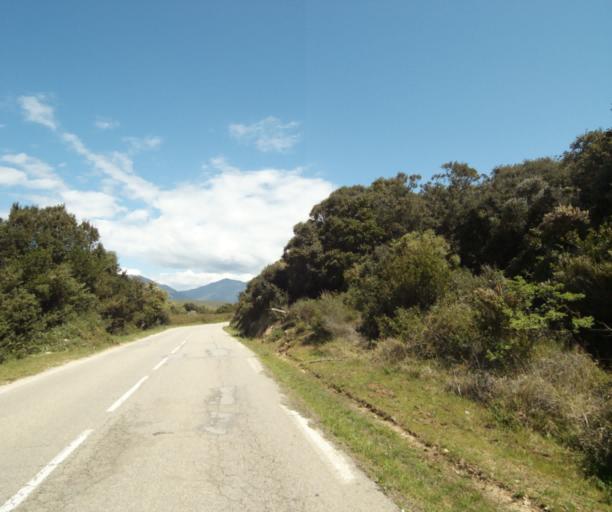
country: FR
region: Corsica
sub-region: Departement de la Corse-du-Sud
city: Propriano
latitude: 41.6487
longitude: 8.8779
